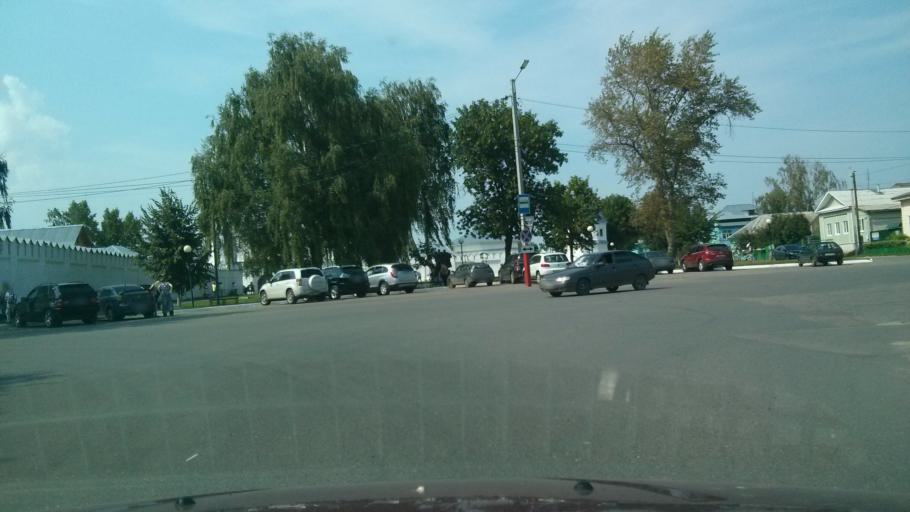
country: RU
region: Vladimir
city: Murom
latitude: 55.5814
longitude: 42.0549
